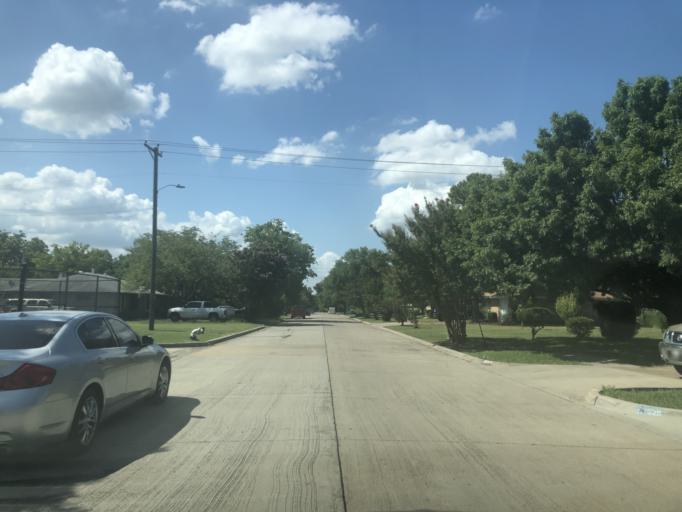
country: US
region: Texas
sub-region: Dallas County
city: Grand Prairie
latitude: 32.7340
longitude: -97.0038
